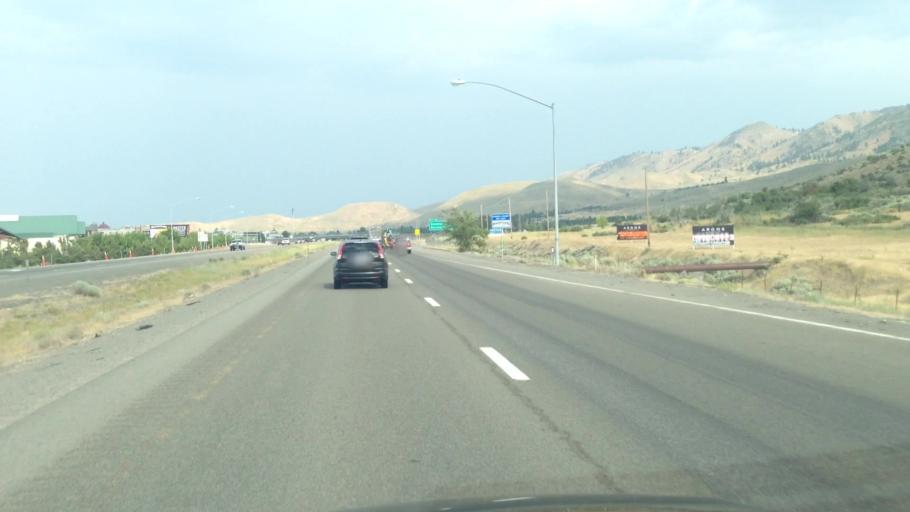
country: US
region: Nevada
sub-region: Washoe County
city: Verdi
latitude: 39.5123
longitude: -119.9729
